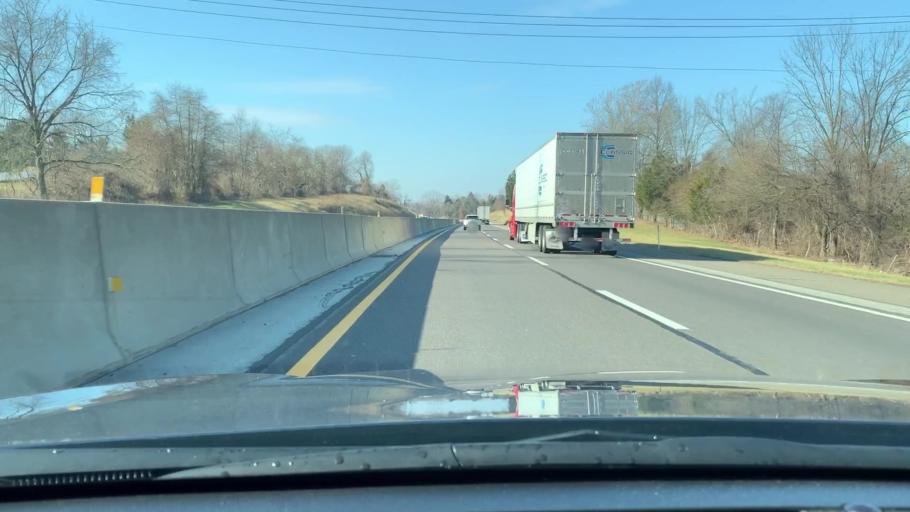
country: US
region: Pennsylvania
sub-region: Chester County
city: Chester Springs
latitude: 40.0652
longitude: -75.6094
